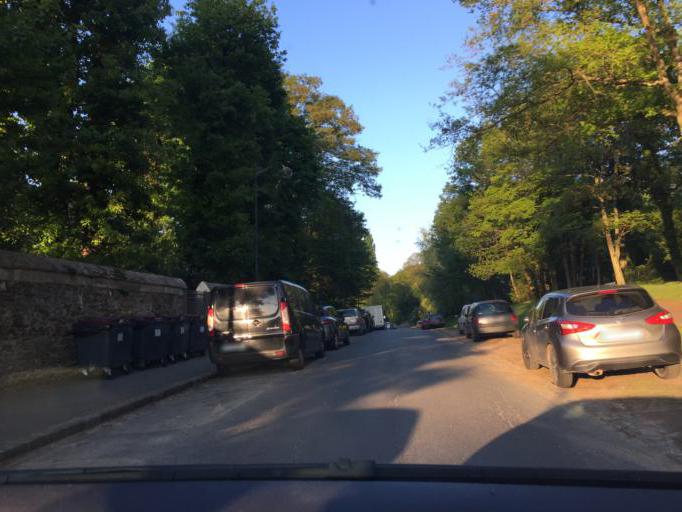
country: FR
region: Ile-de-France
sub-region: Departement de l'Essonne
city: Orsay
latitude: 48.6964
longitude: 2.1953
